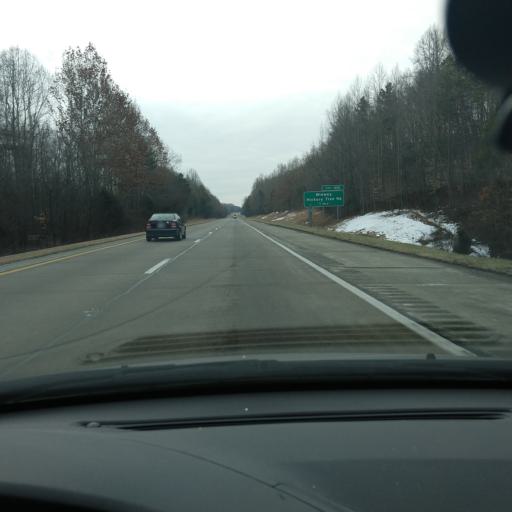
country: US
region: North Carolina
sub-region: Davidson County
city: Midway
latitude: 35.9882
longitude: -80.2372
